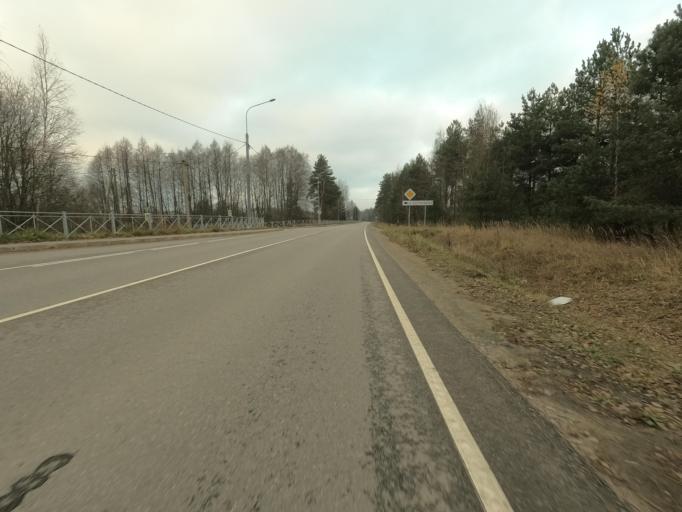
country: RU
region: Leningrad
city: Pavlovo
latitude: 59.8040
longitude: 30.9589
